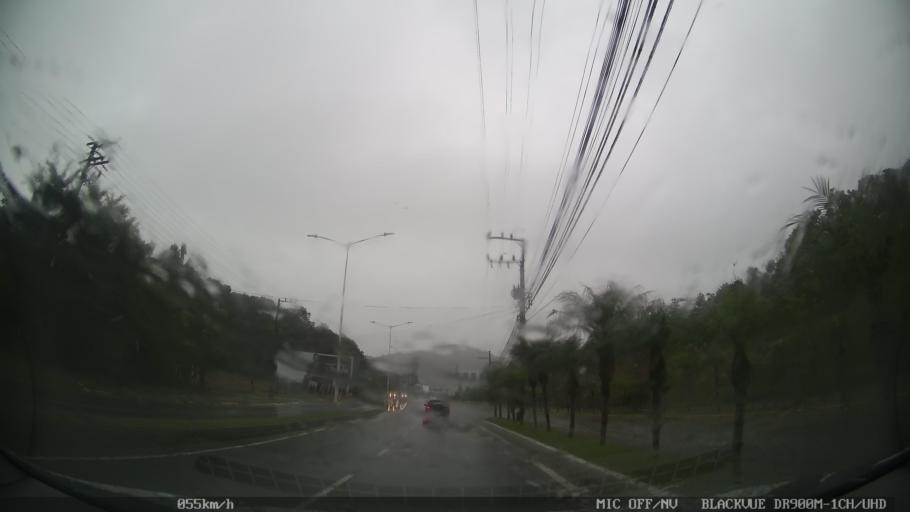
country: BR
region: Santa Catarina
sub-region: Itajai
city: Itajai
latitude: -26.9414
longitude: -48.6413
